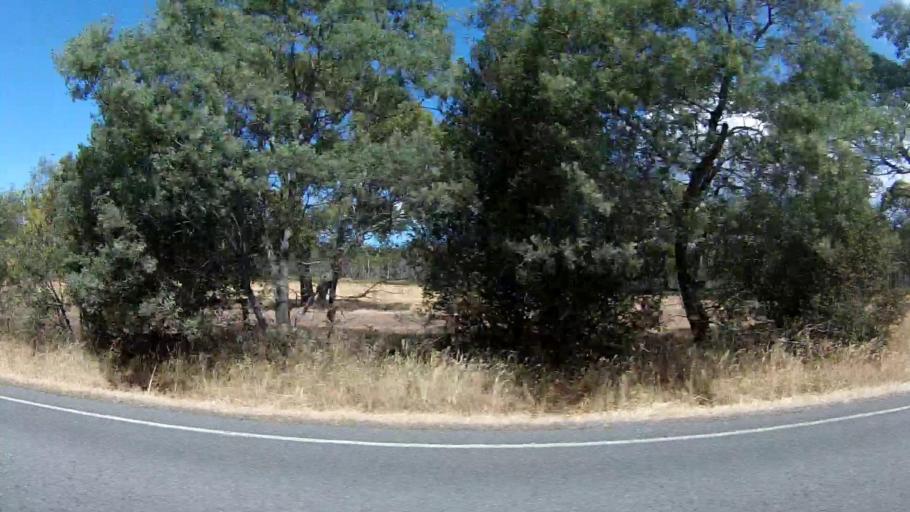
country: AU
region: Tasmania
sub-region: Sorell
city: Sorell
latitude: -42.6073
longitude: 147.7045
